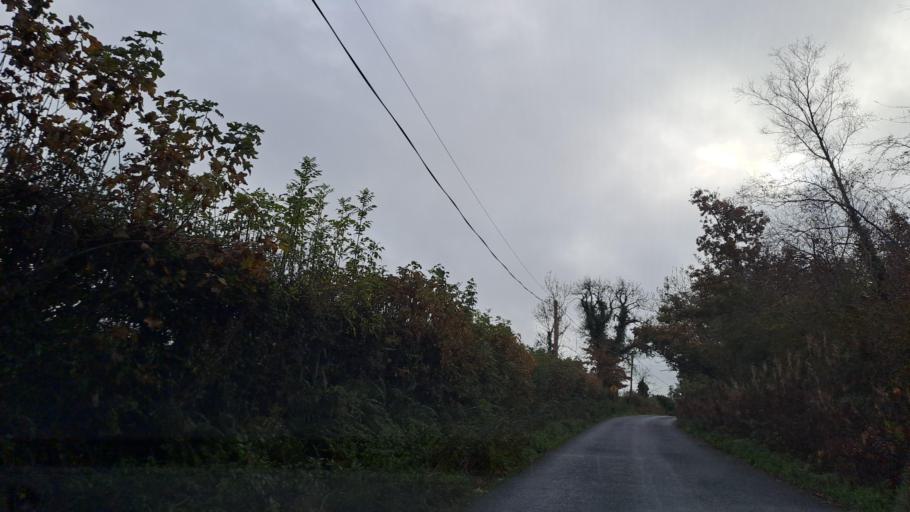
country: IE
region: Ulster
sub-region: An Cabhan
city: Bailieborough
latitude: 53.9393
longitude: -6.9766
